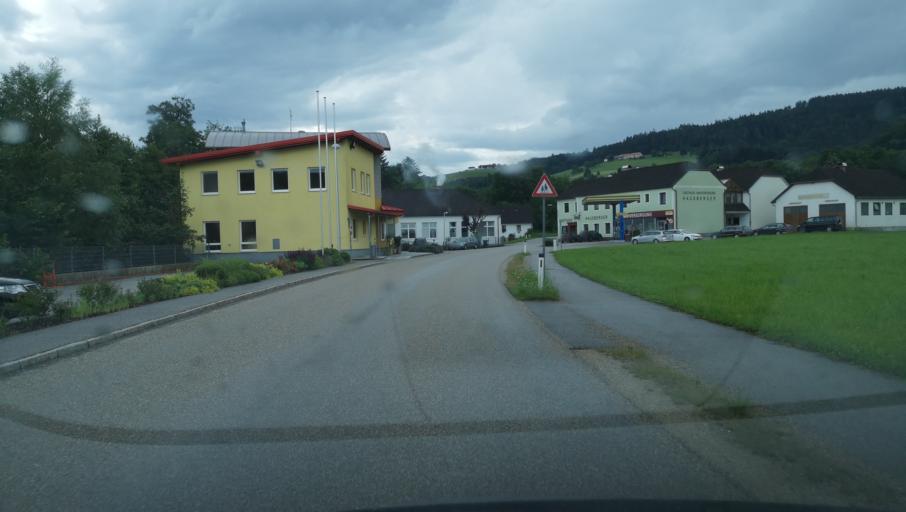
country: AT
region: Lower Austria
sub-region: Politischer Bezirk Amstetten
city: Neuhofen an der Ybbs
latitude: 48.0296
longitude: 14.8378
